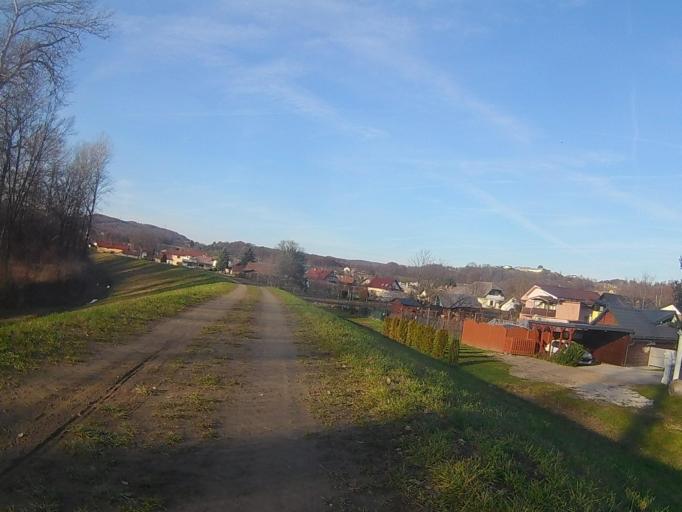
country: SI
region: Duplek
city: Spodnji Duplek
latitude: 46.5037
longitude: 15.7410
